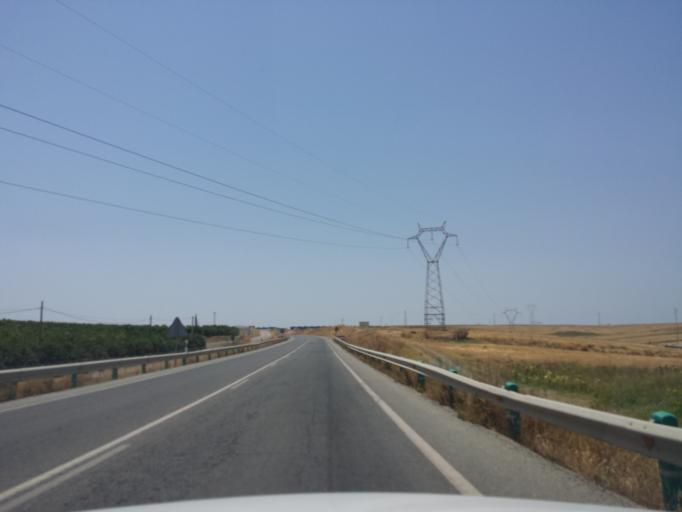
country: ES
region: Andalusia
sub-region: Provincia de Sevilla
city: Acala del Rio
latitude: 37.5313
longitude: -5.9625
